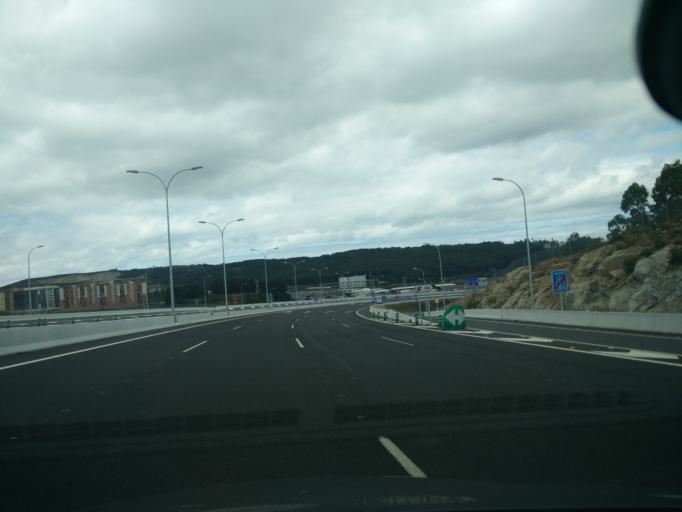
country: ES
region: Galicia
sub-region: Provincia da Coruna
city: Culleredo
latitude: 43.3252
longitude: -8.4200
